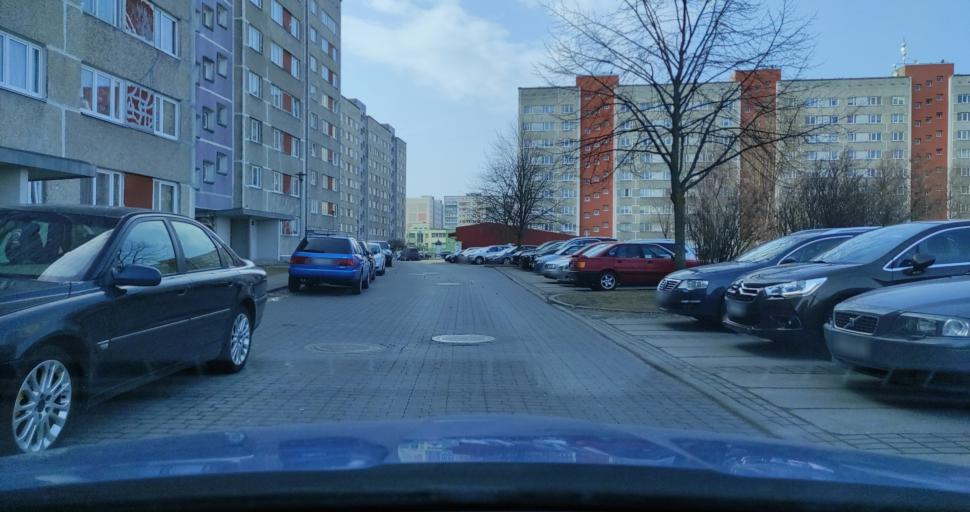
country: LV
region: Ventspils
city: Ventspils
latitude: 57.3822
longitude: 21.5525
